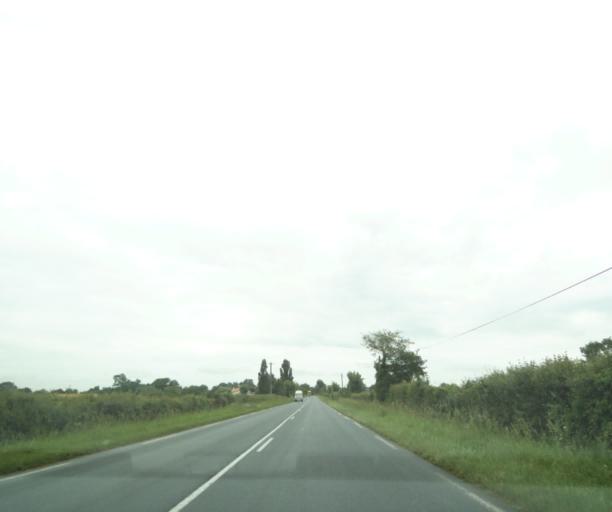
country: FR
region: Poitou-Charentes
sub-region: Departement des Deux-Sevres
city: Viennay
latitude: 46.7051
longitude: -0.2389
